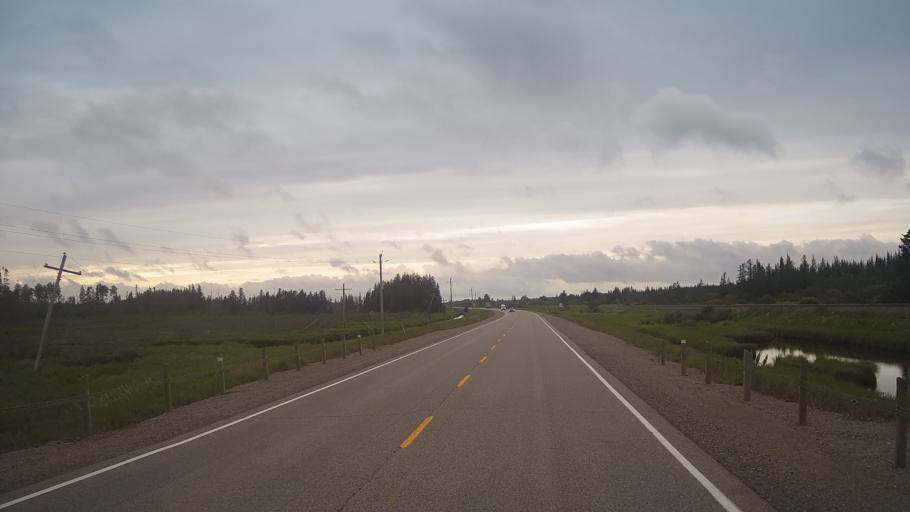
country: CA
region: Ontario
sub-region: Thunder Bay District
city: Thunder Bay
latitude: 48.8717
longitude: -89.9768
